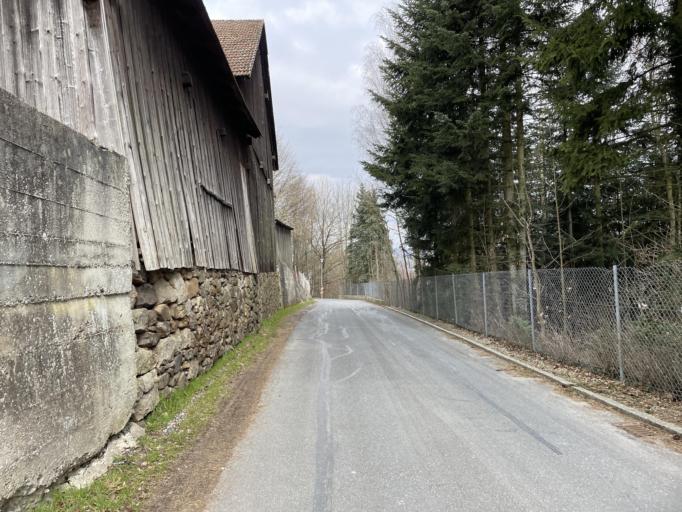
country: DE
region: Bavaria
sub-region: Upper Palatinate
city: Runding
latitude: 49.2157
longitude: 12.7644
